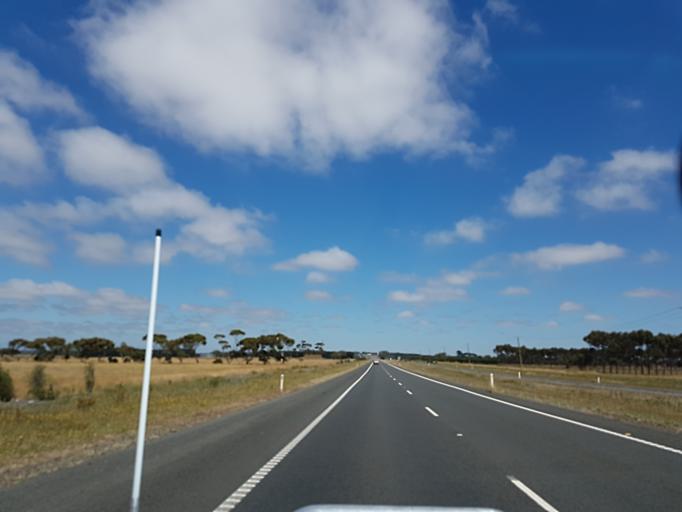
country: AU
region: Victoria
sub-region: Greater Geelong
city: Wandana Heights
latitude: -38.2135
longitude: 144.1547
